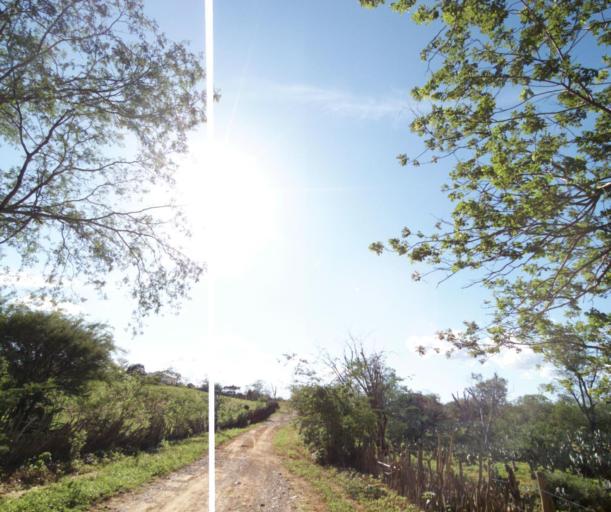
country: BR
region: Bahia
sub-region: Tanhacu
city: Tanhacu
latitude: -14.1825
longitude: -40.9291
